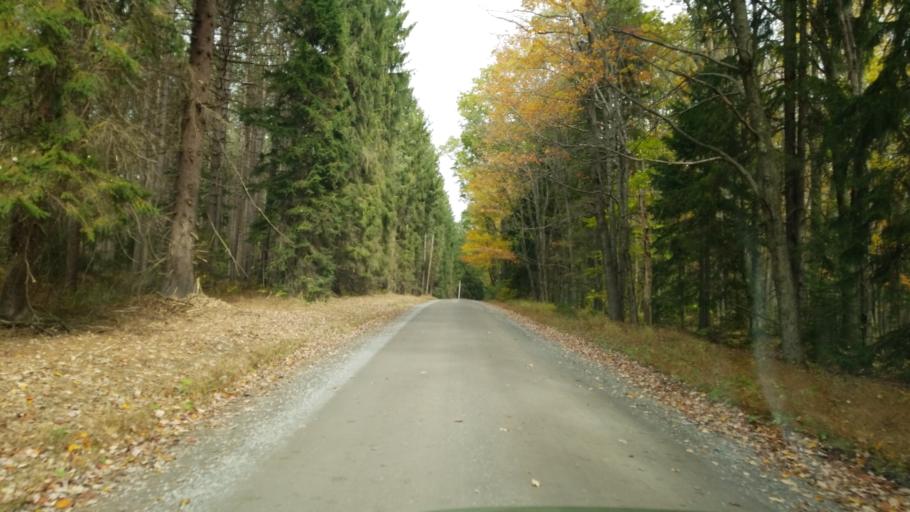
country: US
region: Pennsylvania
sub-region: Clearfield County
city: Clearfield
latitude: 41.1892
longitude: -78.4428
